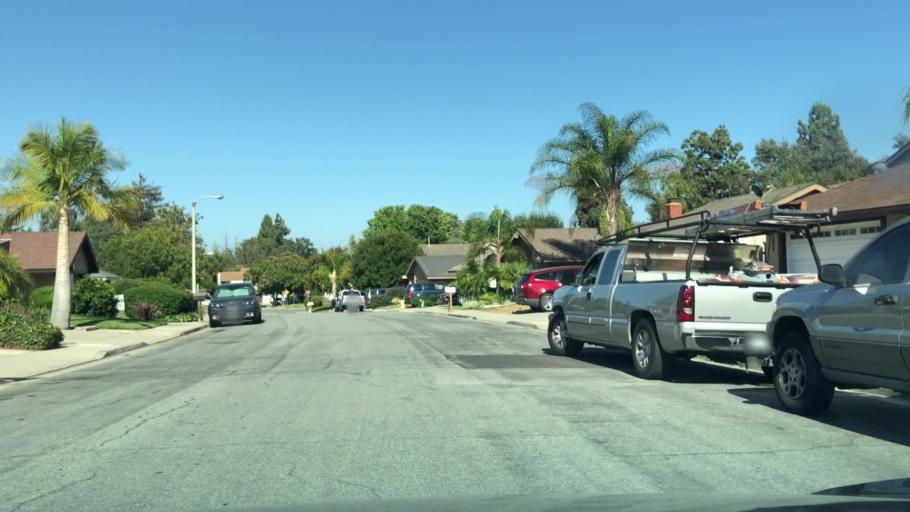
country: US
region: California
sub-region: Ventura County
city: Casa Conejo
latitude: 34.1793
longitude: -118.9570
